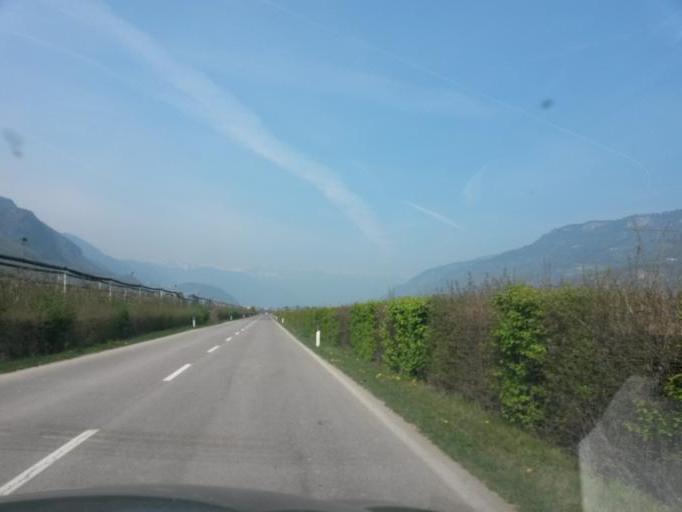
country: IT
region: Trentino-Alto Adige
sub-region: Bolzano
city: San Paolo
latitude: 46.4974
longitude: 11.2564
